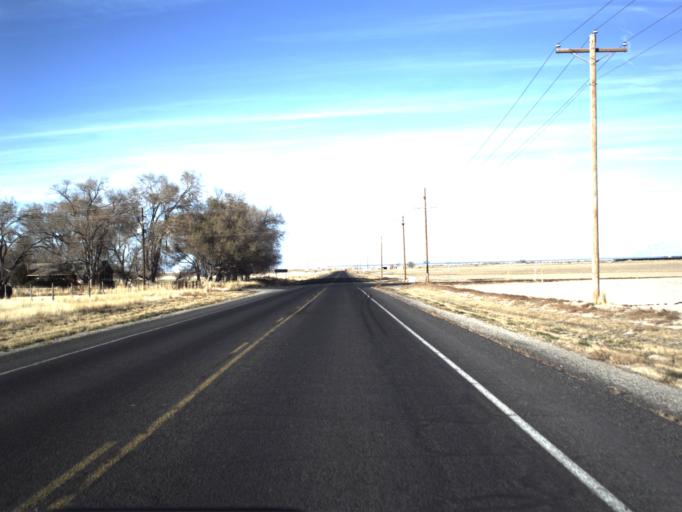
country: US
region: Utah
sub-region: Tooele County
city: Erda
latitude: 40.5998
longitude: -112.3706
